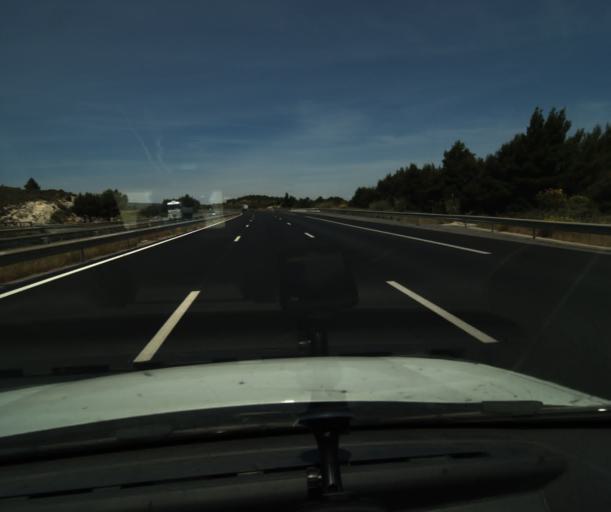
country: FR
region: Languedoc-Roussillon
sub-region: Departement de l'Aude
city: Portel-des-Corbieres
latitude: 43.0677
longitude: 2.9376
